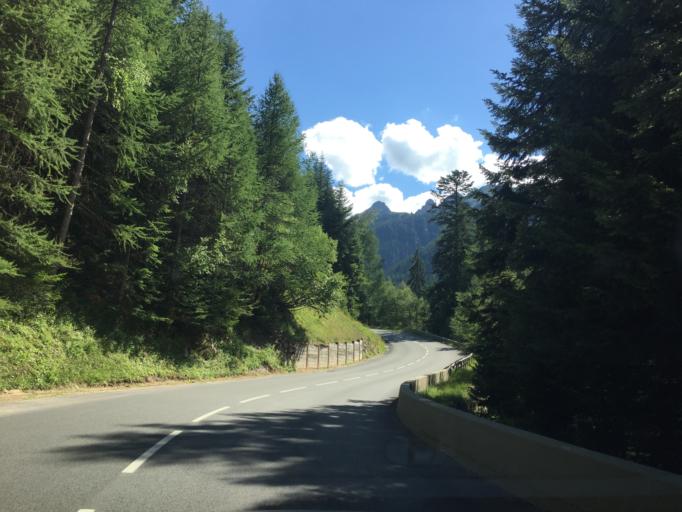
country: FR
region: Rhone-Alpes
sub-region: Departement de la Savoie
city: Modane
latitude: 45.1852
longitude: 6.6605
